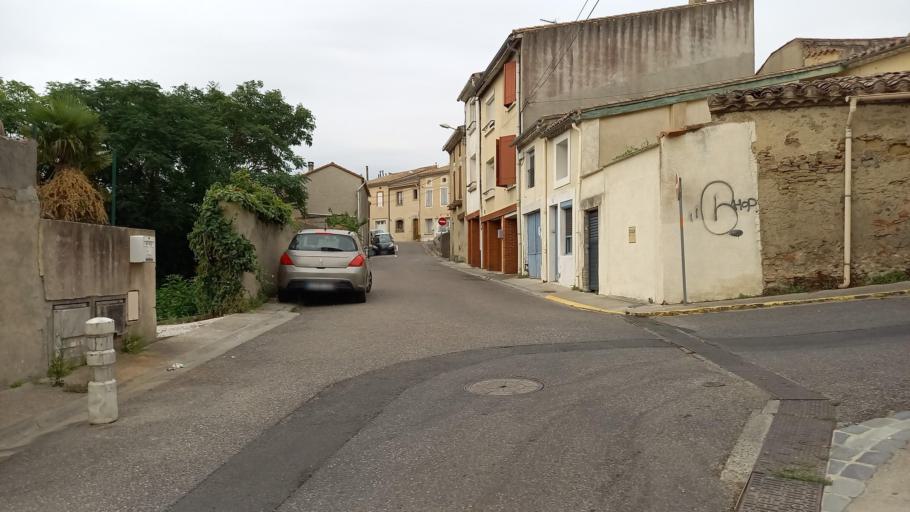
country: FR
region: Languedoc-Roussillon
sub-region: Departement de l'Aude
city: Castelnaudary
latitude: 43.3152
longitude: 1.9594
